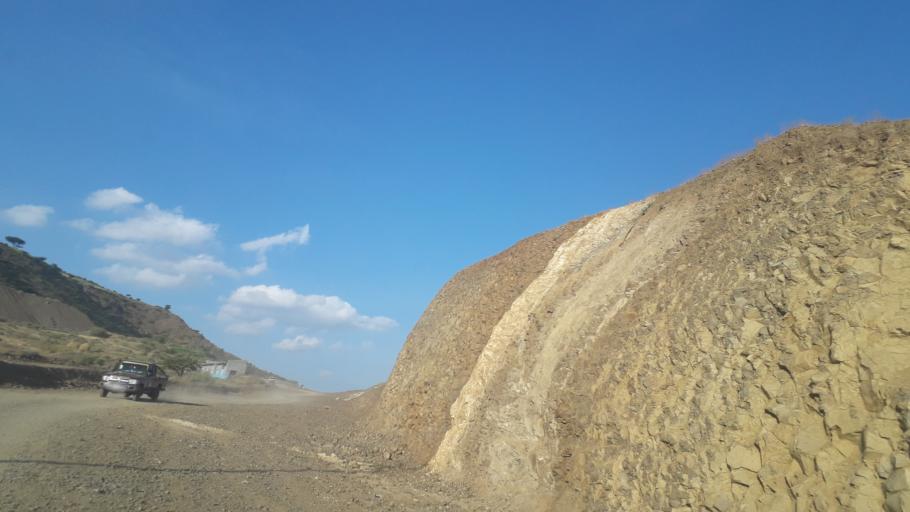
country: ET
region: Amhara
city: Dese
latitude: 11.5218
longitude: 39.2488
